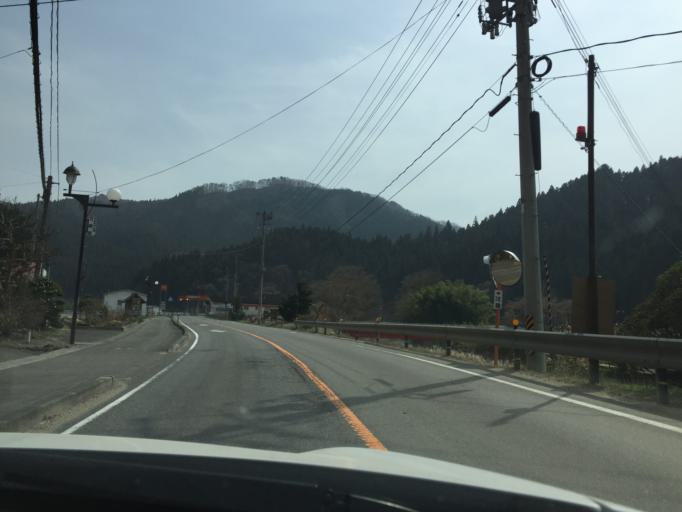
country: JP
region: Fukushima
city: Ishikawa
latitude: 37.0594
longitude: 140.5839
